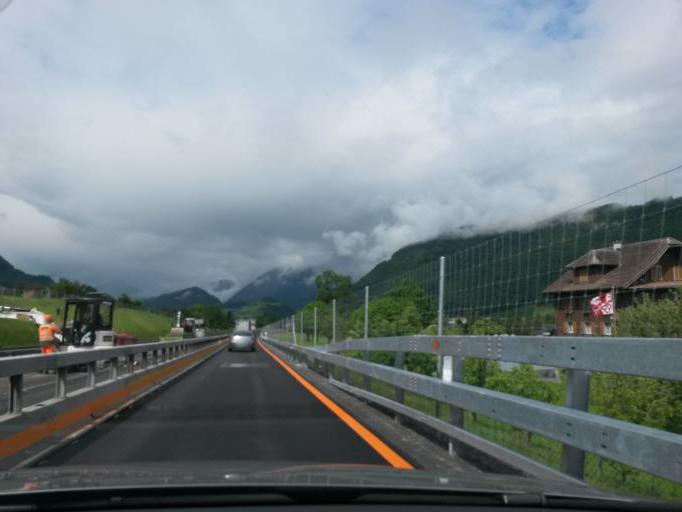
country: CH
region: Nidwalden
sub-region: Nidwalden
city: Ennetburgen
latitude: 46.9697
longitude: 8.4082
